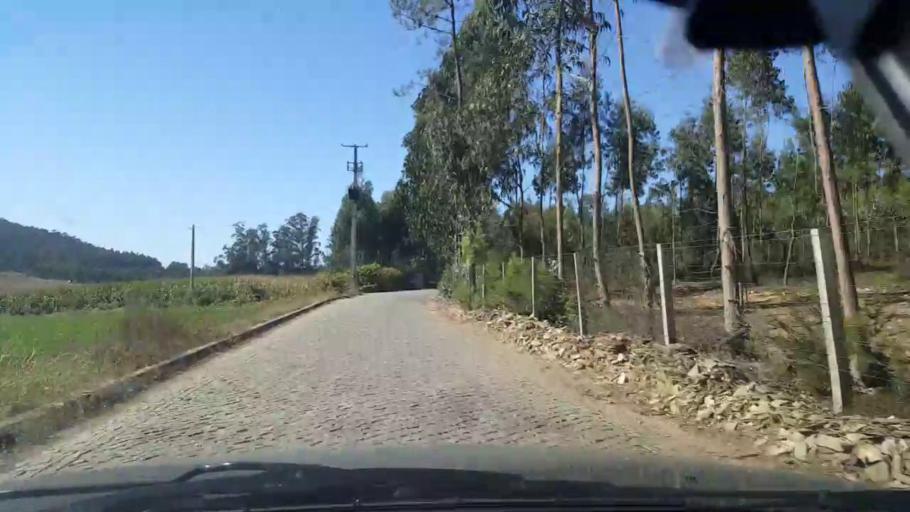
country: PT
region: Braga
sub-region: Vila Nova de Famalicao
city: Ribeirao
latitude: 41.3909
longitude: -8.6360
